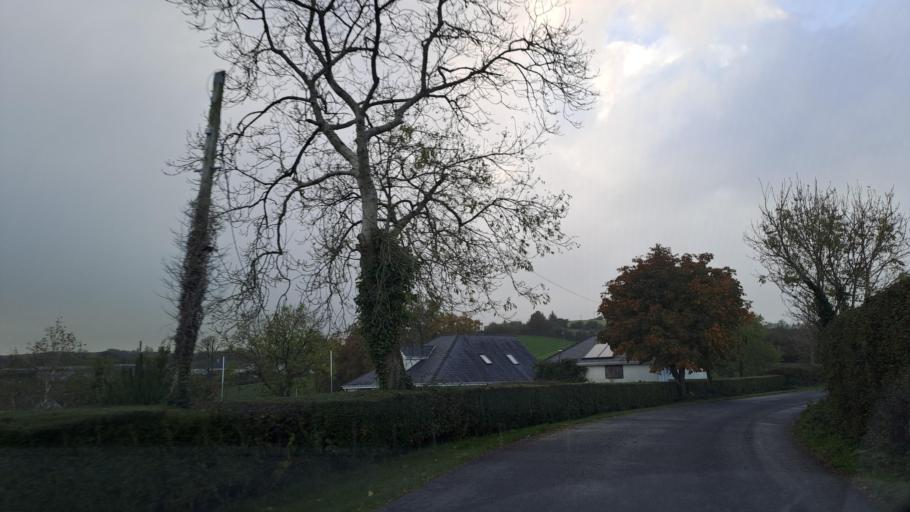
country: IE
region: Ulster
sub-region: An Cabhan
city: Kingscourt
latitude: 53.9687
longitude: -6.7856
